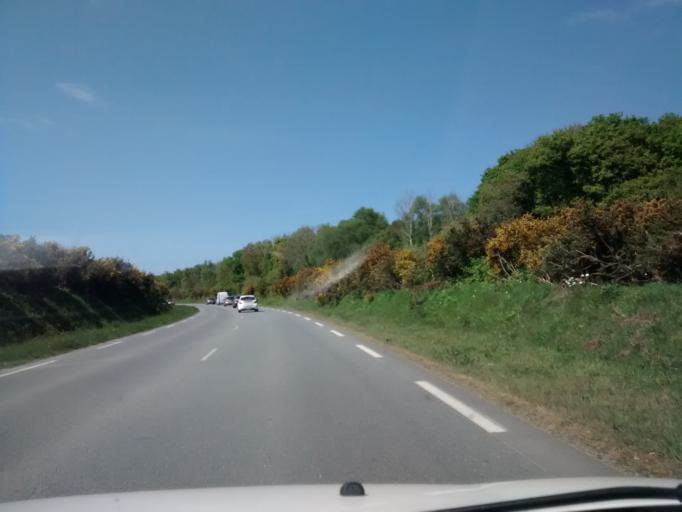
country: FR
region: Brittany
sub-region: Departement d'Ille-et-Vilaine
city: Pleurtuit
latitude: 48.5638
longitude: -2.0552
